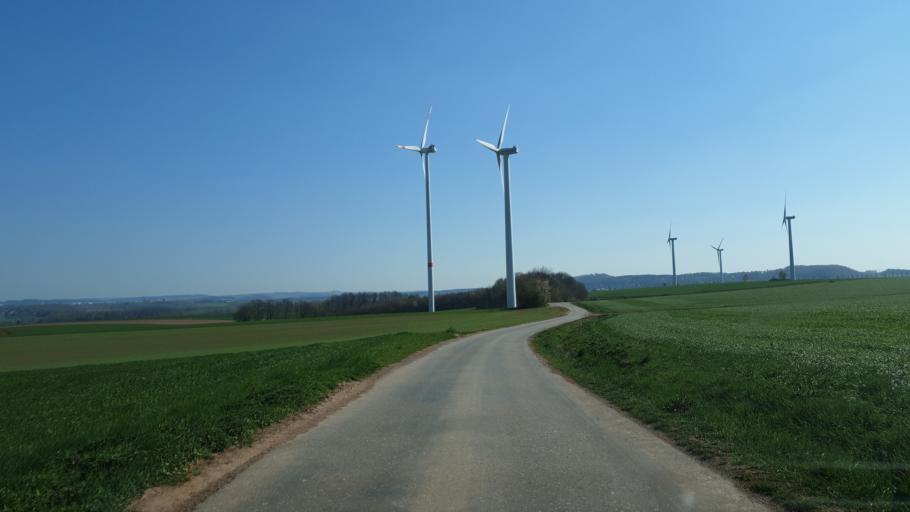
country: DE
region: Saxony
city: Hohndorf
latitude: 50.7643
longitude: 12.6849
